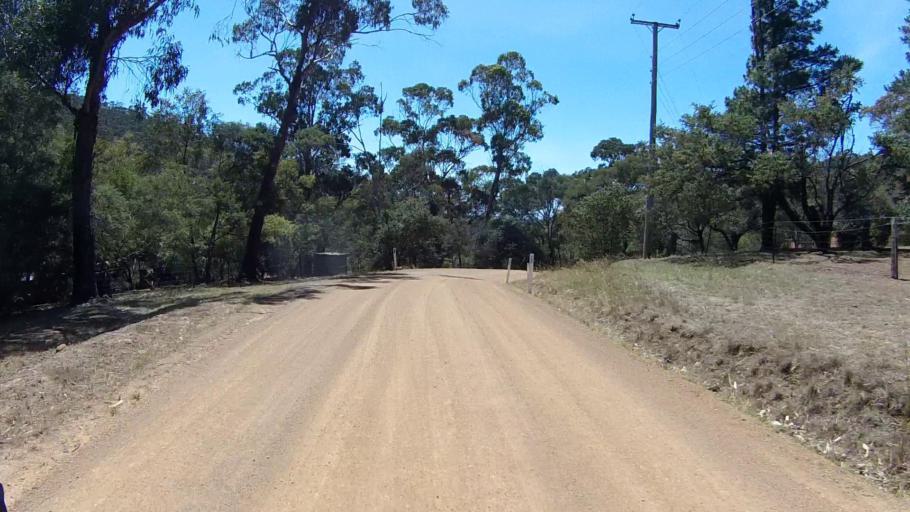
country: AU
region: Tasmania
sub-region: Clarence
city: Cambridge
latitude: -42.8519
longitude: 147.4347
